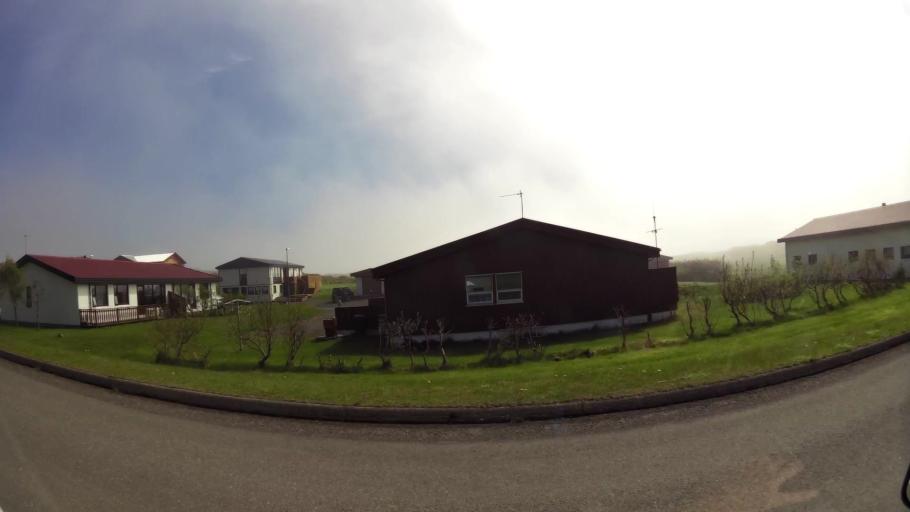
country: IS
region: East
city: Reydarfjoerdur
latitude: 64.6551
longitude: -14.2900
